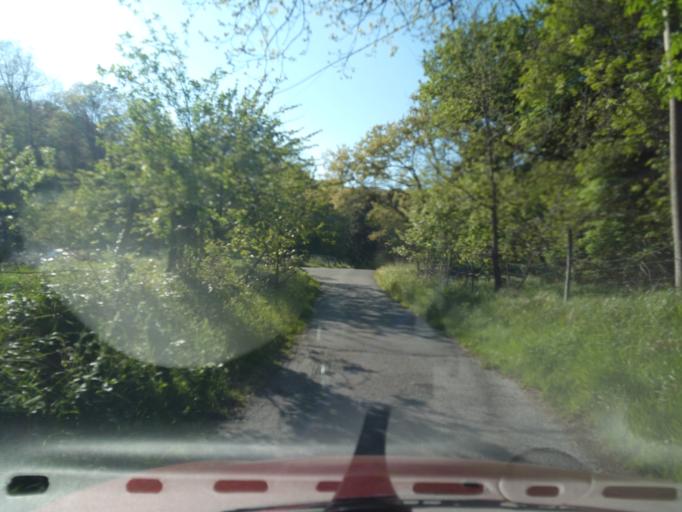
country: IT
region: Liguria
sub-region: Provincia di Genova
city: Sciarborasca
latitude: 44.3963
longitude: 8.5883
